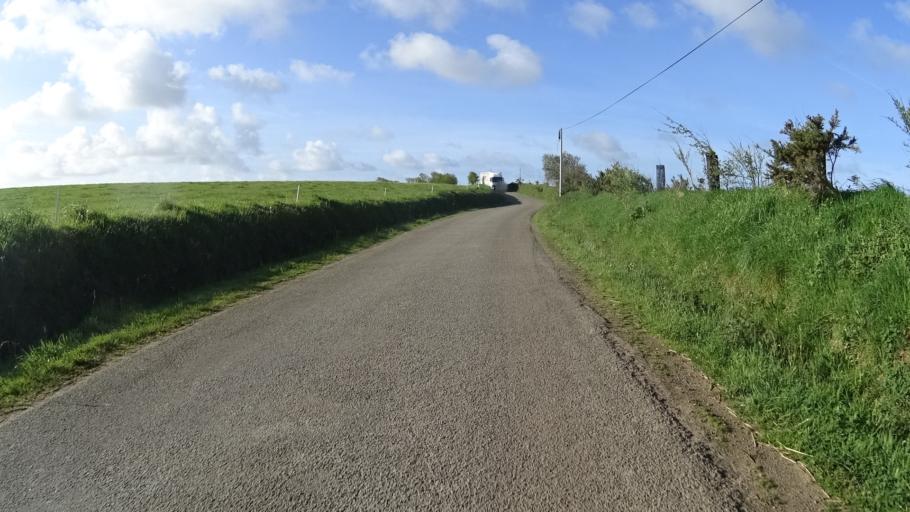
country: FR
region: Brittany
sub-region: Departement du Finistere
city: Ploumoguer
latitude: 48.4193
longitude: -4.6889
